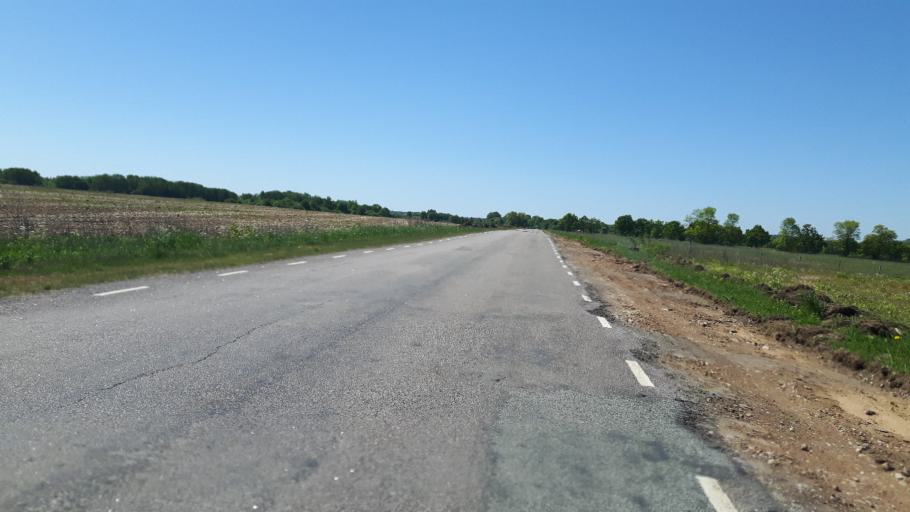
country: EE
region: Ida-Virumaa
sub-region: Narva-Joesuu linn
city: Narva-Joesuu
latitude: 59.3998
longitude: 27.9335
